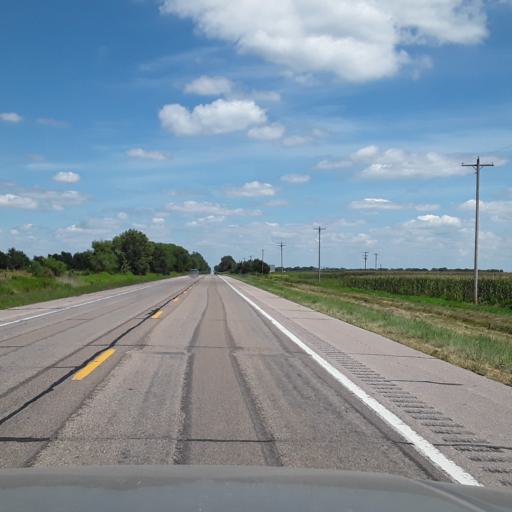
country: US
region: Nebraska
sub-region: Platte County
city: Columbus
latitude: 41.3726
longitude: -97.5302
